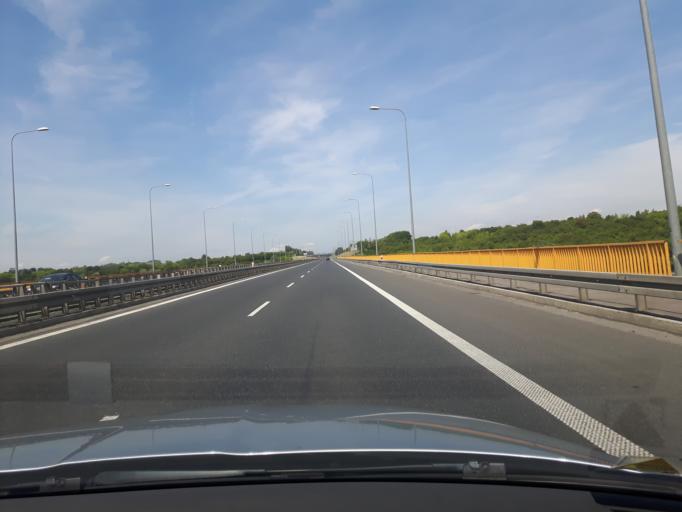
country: PL
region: Masovian Voivodeship
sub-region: Powiat nowodworski
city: Zakroczym
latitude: 52.4268
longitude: 20.6563
